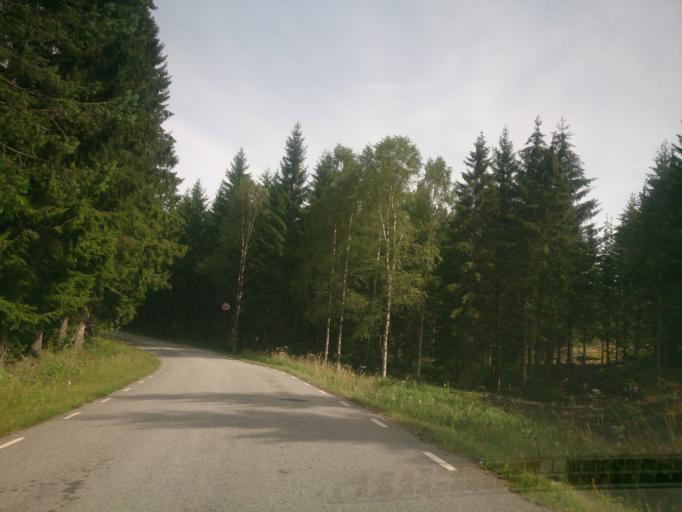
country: SE
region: OEstergoetland
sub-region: Soderkopings Kommun
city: Soederkoeping
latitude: 58.3096
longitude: 16.2910
